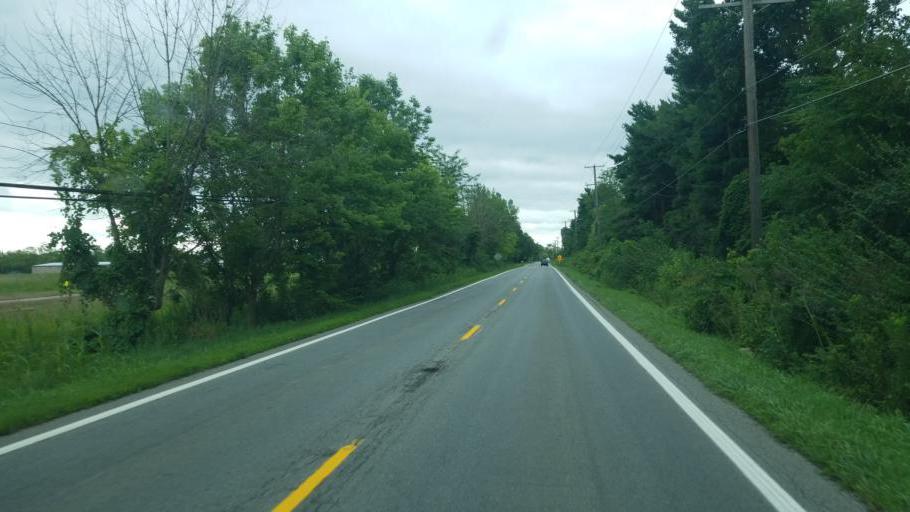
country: US
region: Ohio
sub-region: Franklin County
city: Grove City
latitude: 39.8522
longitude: -83.0282
